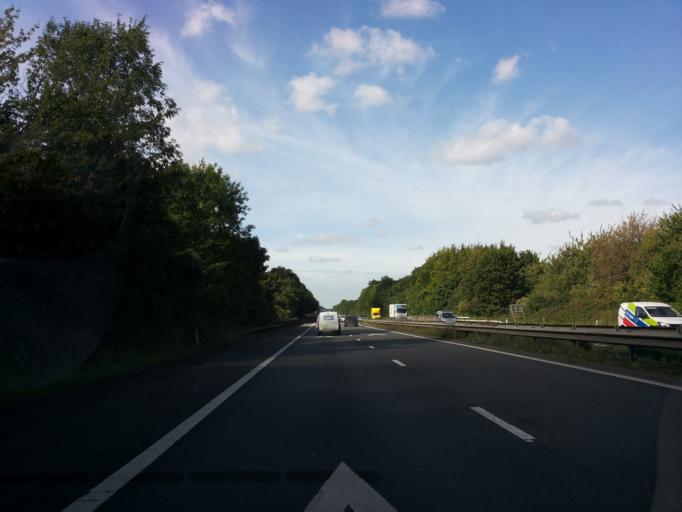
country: GB
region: England
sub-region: Kent
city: Sittingbourne
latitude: 51.2998
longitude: 0.7338
